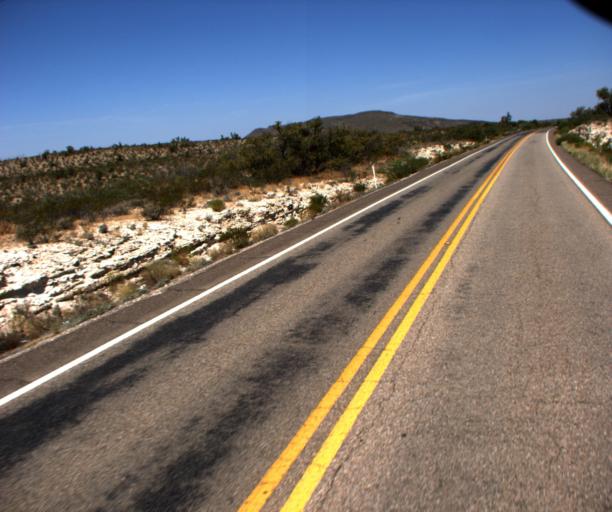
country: US
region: Arizona
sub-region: Gila County
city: Peridot
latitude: 33.2711
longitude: -110.3208
